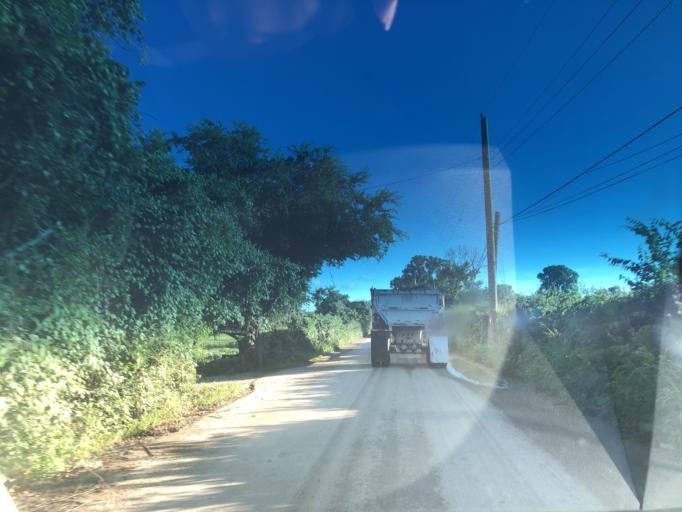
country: US
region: Texas
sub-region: Dallas County
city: Grand Prairie
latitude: 32.7911
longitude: -97.0091
